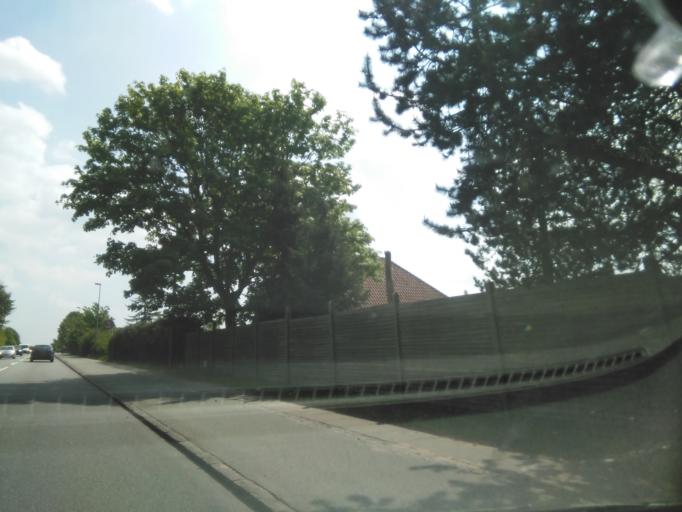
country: DK
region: Central Jutland
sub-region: Skanderborg Kommune
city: Skanderborg
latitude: 56.0397
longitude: 9.9431
